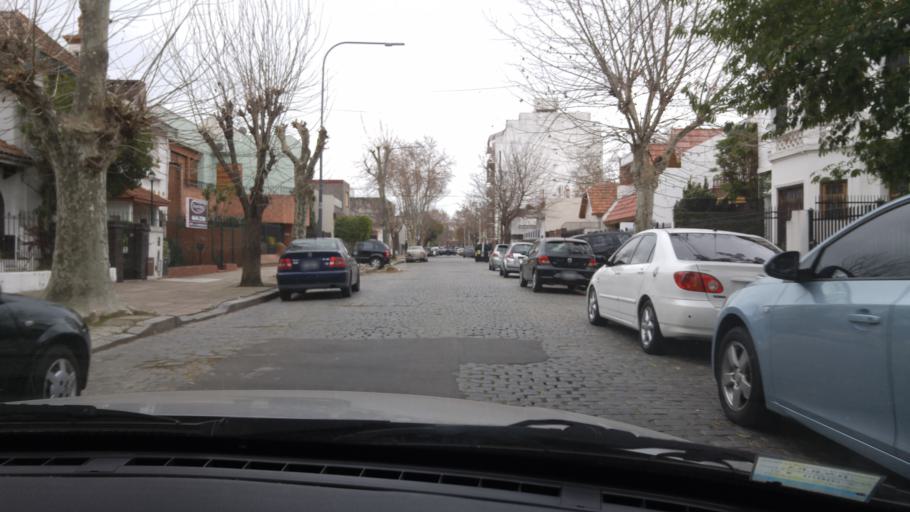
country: AR
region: Buenos Aires
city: Caseros
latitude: -34.6282
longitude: -58.5260
